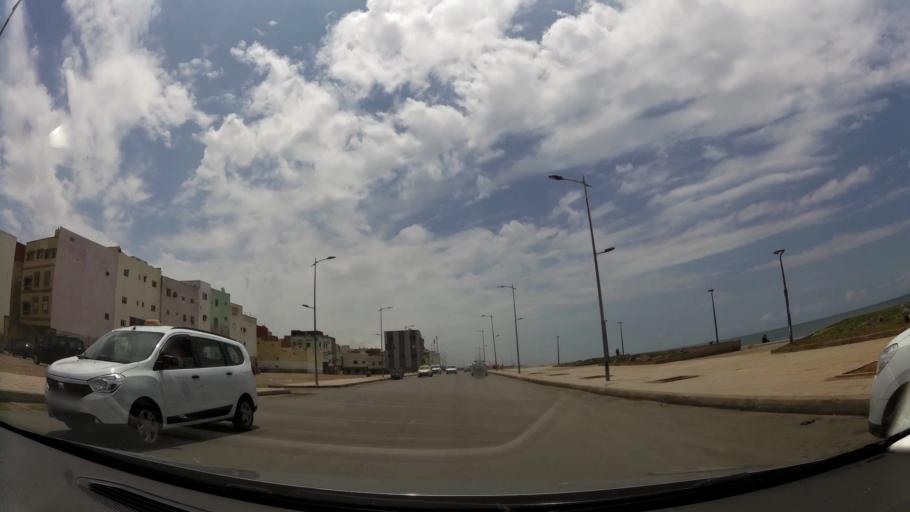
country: MA
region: Rabat-Sale-Zemmour-Zaer
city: Sale
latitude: 34.0514
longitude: -6.8249
